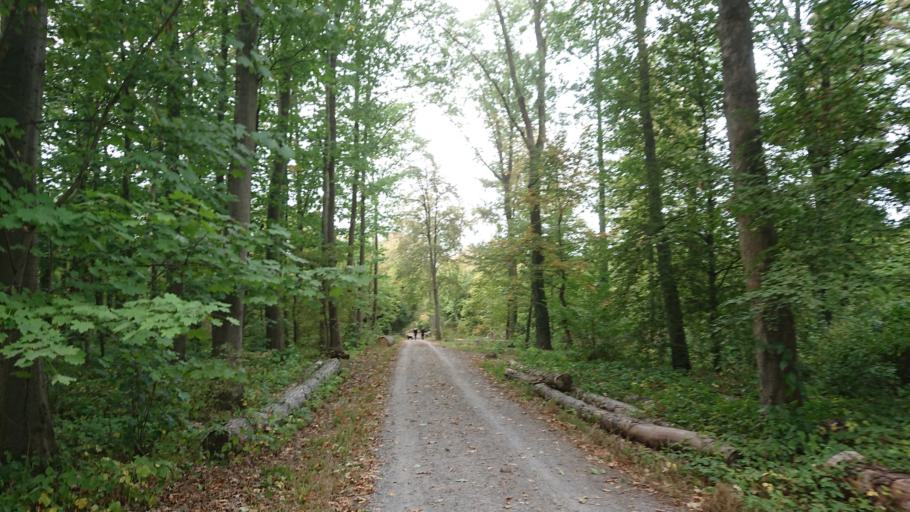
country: DE
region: Baden-Wuerttemberg
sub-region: Karlsruhe Region
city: Karlsruhe
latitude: 48.9843
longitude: 8.4146
